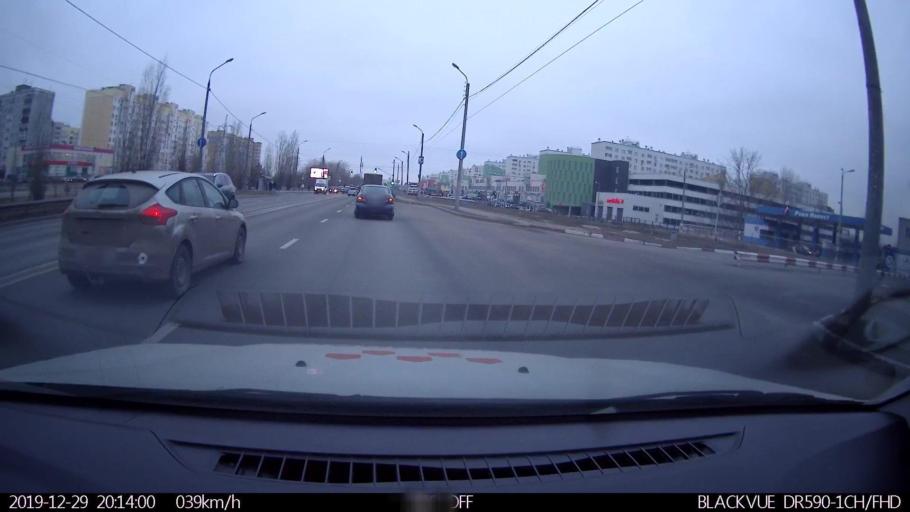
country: RU
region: Nizjnij Novgorod
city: Nizhniy Novgorod
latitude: 56.3390
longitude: 43.9191
